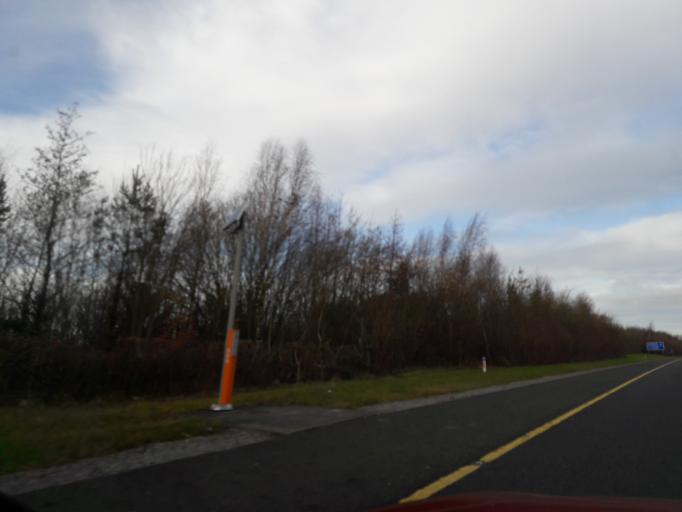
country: IE
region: Leinster
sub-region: Lu
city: Drogheda
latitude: 53.6715
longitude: -6.3492
